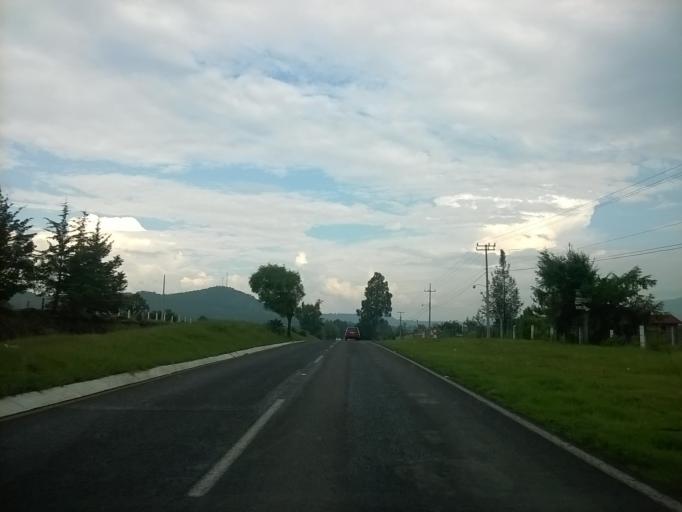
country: MX
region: Michoacan
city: Cuanajo
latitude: 19.5342
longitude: -101.5040
